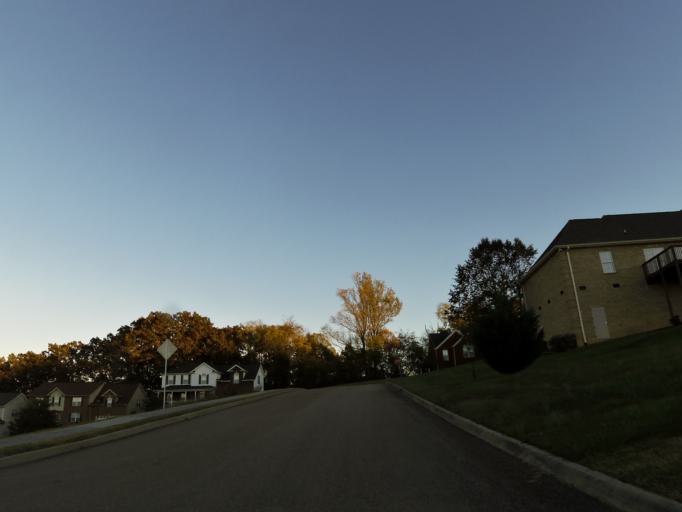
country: US
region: Tennessee
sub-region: Knox County
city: Knoxville
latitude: 36.0264
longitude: -83.9760
